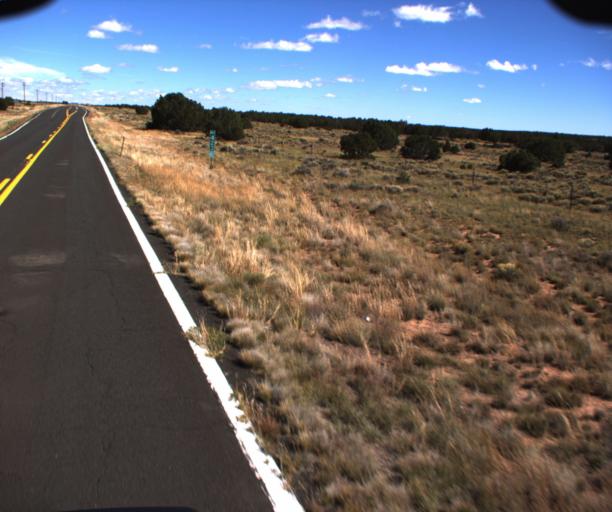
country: US
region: New Mexico
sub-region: McKinley County
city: Zuni Pueblo
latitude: 34.9633
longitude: -109.1529
